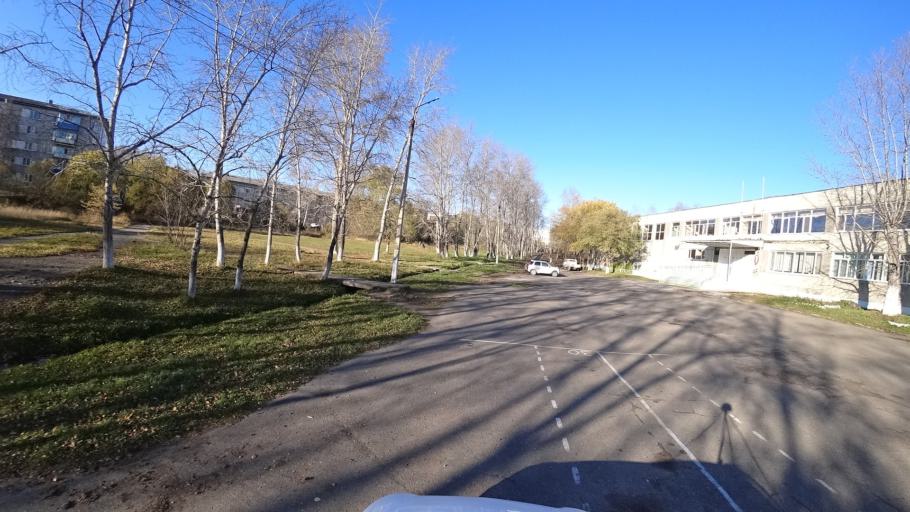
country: RU
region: Khabarovsk Krai
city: Amursk
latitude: 50.2303
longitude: 136.9079
